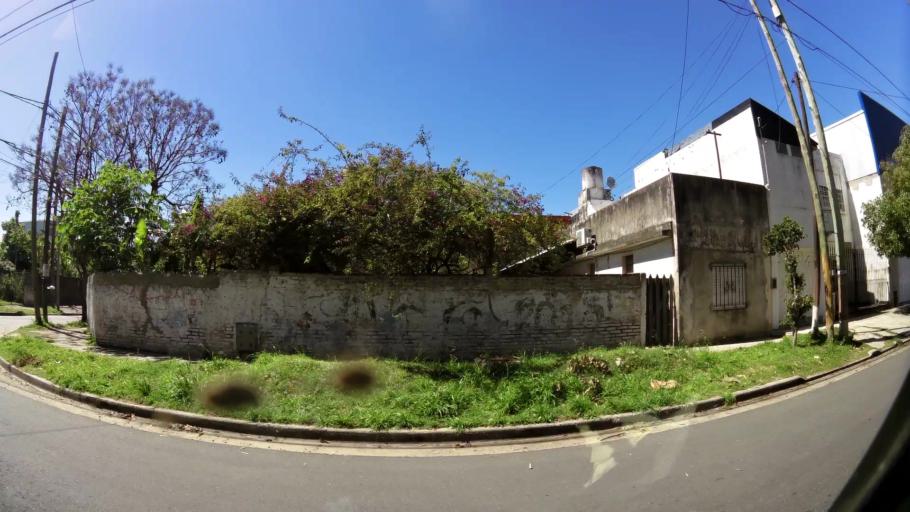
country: AR
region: Buenos Aires
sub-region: Partido de Quilmes
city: Quilmes
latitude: -34.7256
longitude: -58.3101
